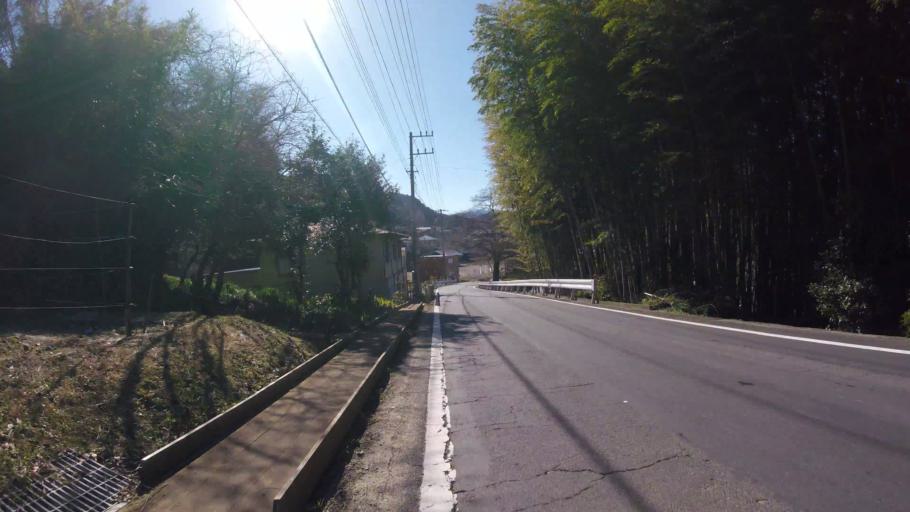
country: JP
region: Shizuoka
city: Ito
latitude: 34.9512
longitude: 138.9426
